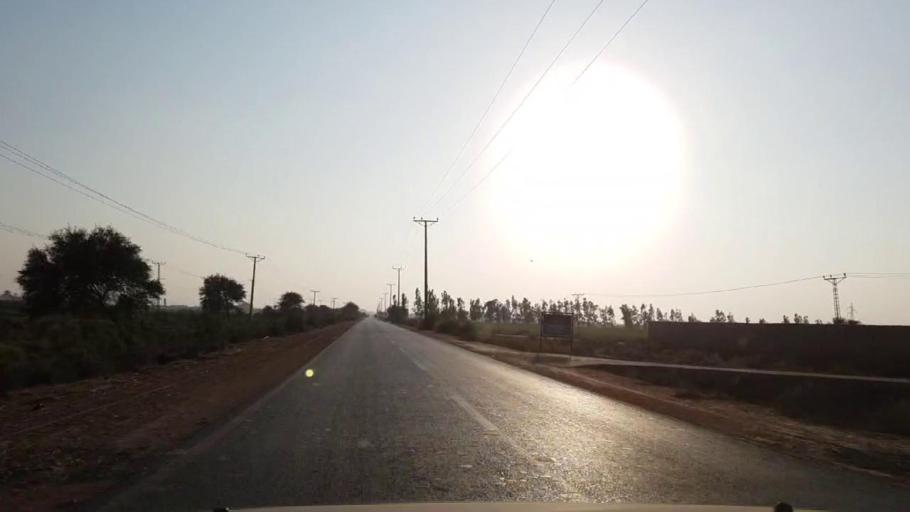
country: PK
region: Sindh
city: Daro Mehar
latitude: 24.6252
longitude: 68.0994
